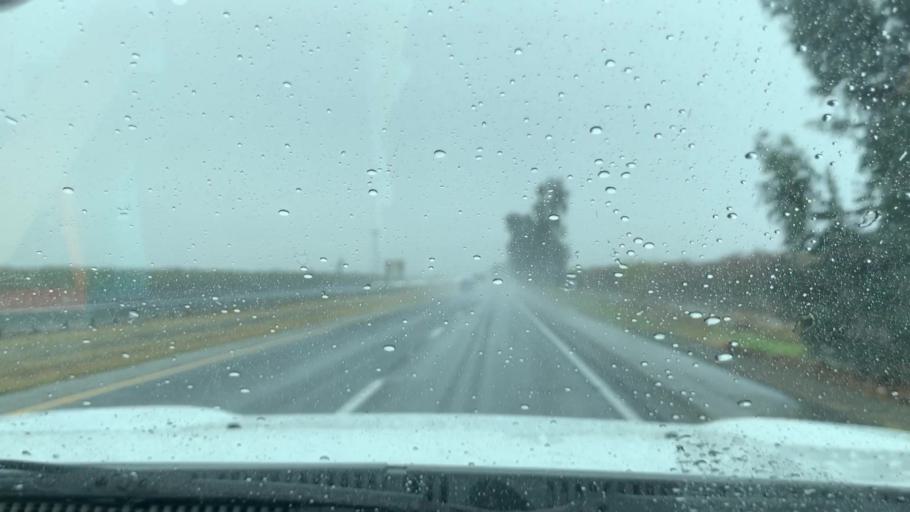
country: US
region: California
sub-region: Tulare County
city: Earlimart
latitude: 35.8567
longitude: -119.2677
